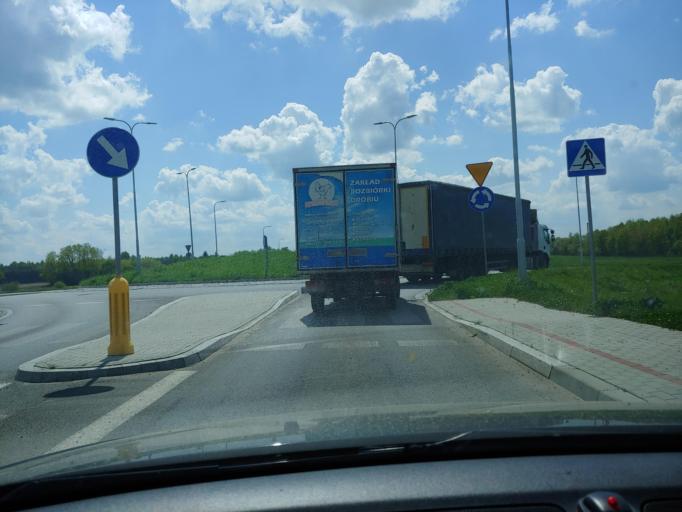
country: PL
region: Subcarpathian Voivodeship
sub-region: Powiat mielecki
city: Radomysl Wielki
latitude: 50.1871
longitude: 21.2642
